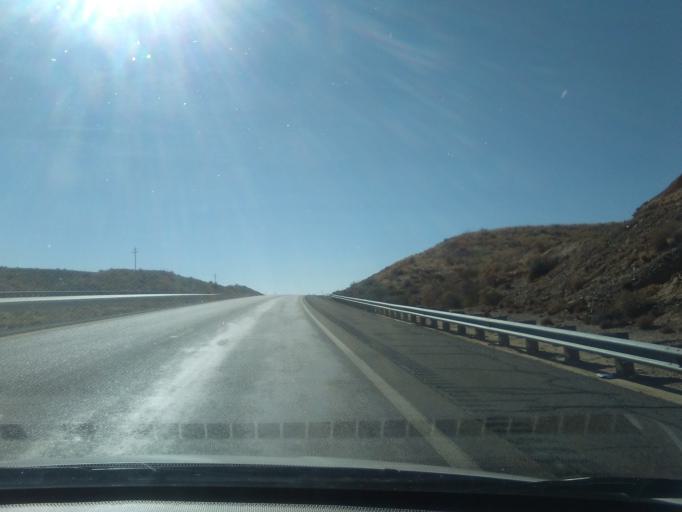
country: US
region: New Mexico
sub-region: Socorro County
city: Socorro
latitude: 34.3307
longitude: -106.8799
